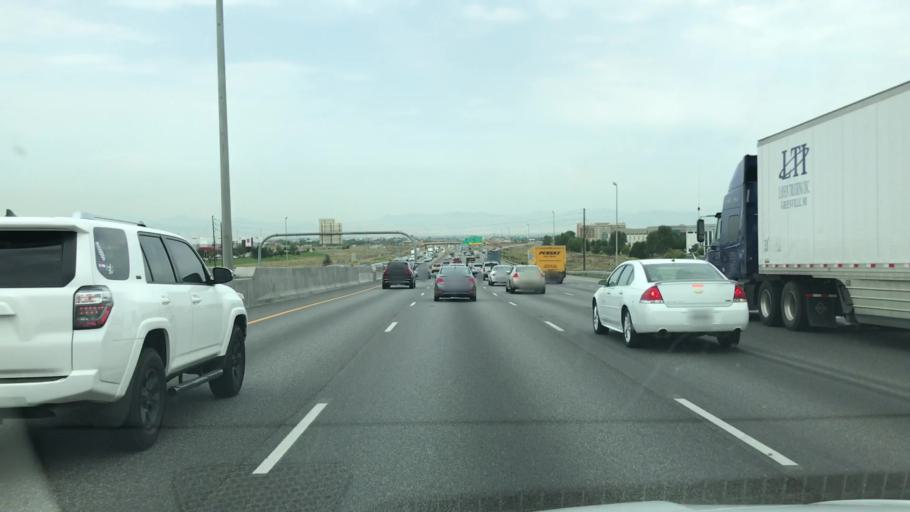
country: US
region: Colorado
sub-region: Adams County
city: Aurora
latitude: 39.7768
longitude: -104.8679
